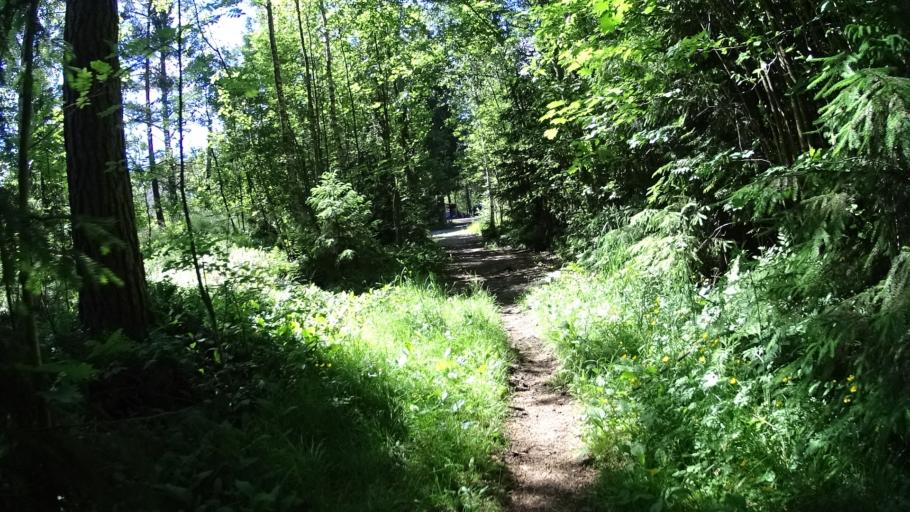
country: FI
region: Uusimaa
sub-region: Helsinki
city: Kilo
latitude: 60.2931
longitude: 24.8238
